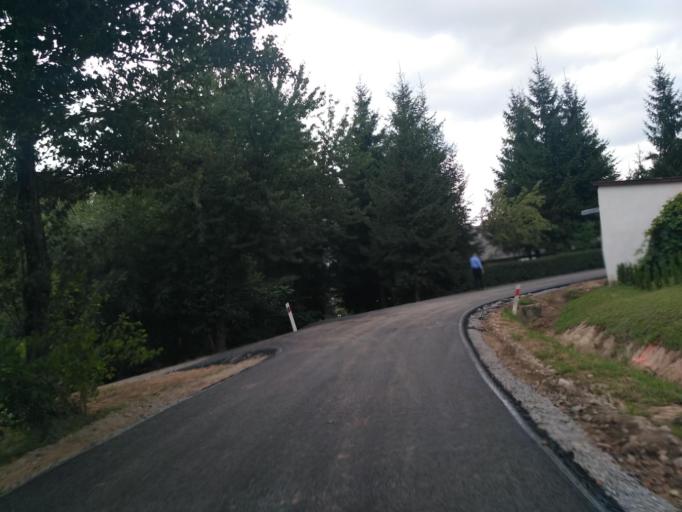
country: PL
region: Subcarpathian Voivodeship
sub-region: Powiat rzeszowski
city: Chmielnik
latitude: 50.0033
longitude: 22.1408
